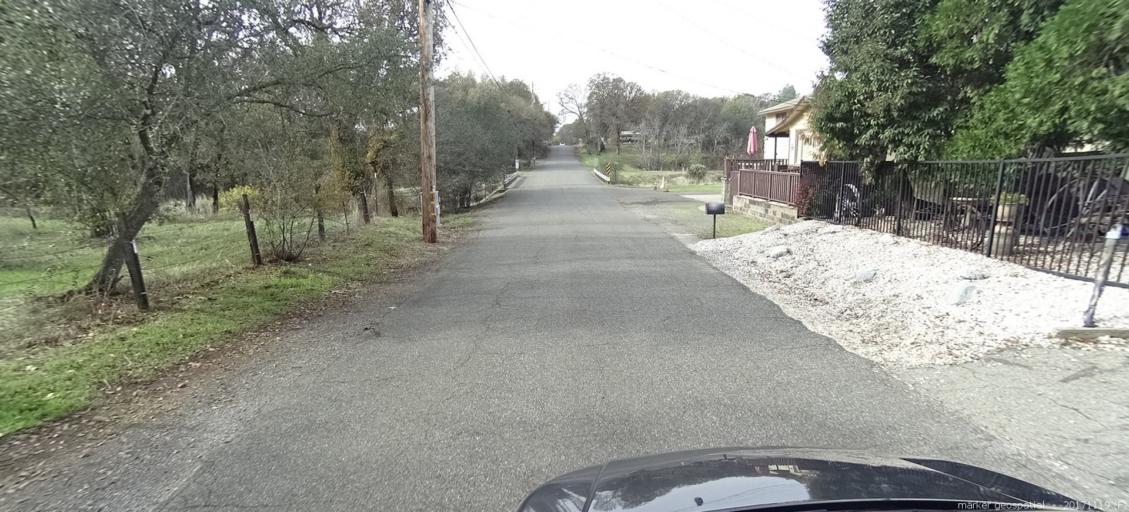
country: US
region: California
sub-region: Shasta County
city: Anderson
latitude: 40.4766
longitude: -122.2943
